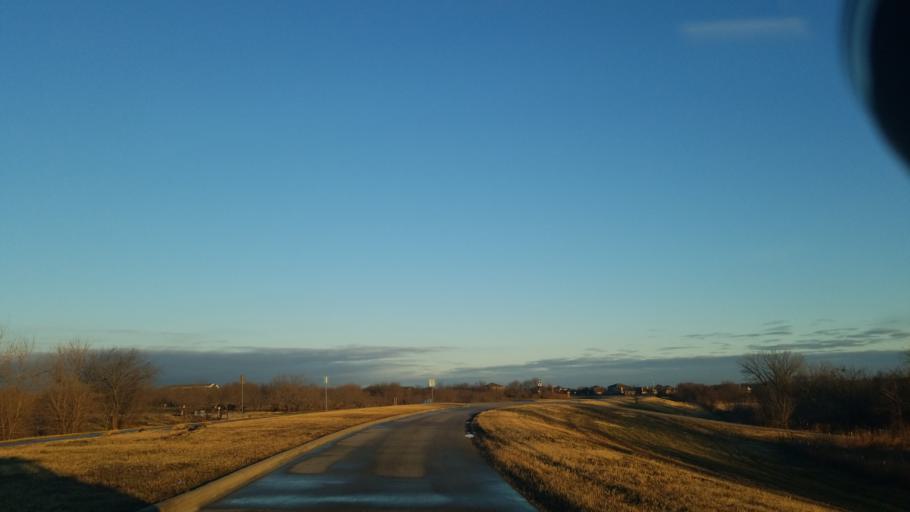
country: US
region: Texas
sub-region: Denton County
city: Argyle
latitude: 33.1648
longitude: -97.1584
